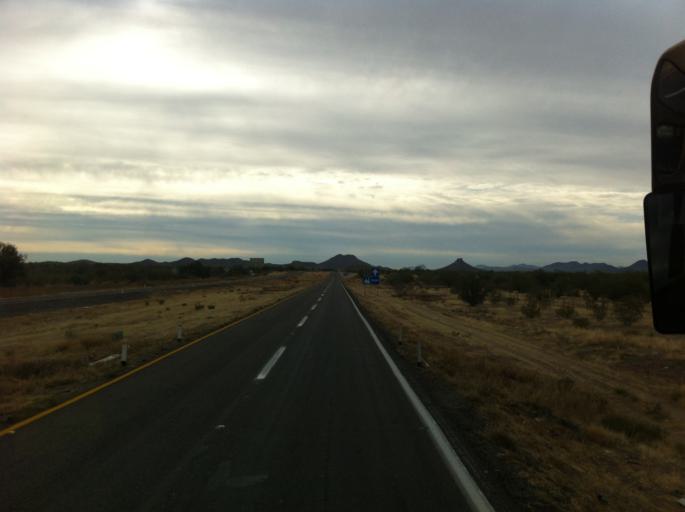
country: MX
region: Sonora
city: Hermosillo
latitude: 28.9423
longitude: -110.9611
